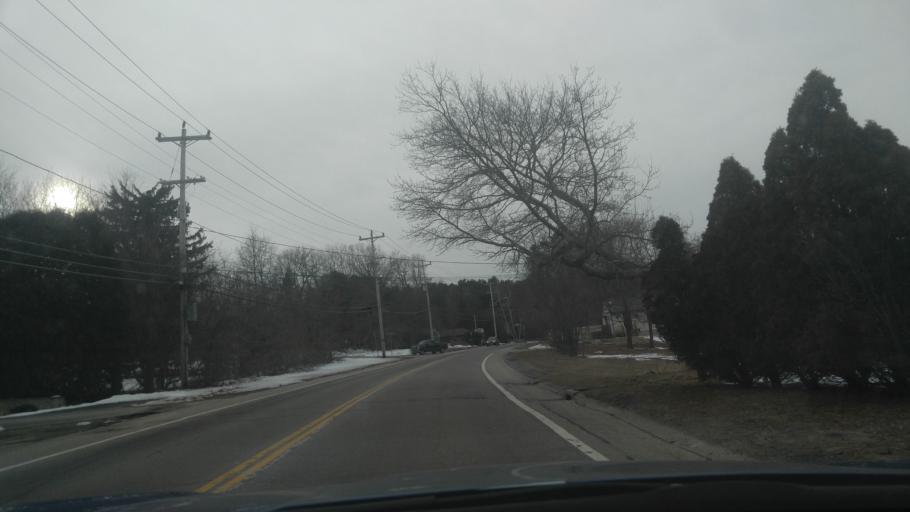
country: US
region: Rhode Island
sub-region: Kent County
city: West Warwick
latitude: 41.6794
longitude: -71.5366
